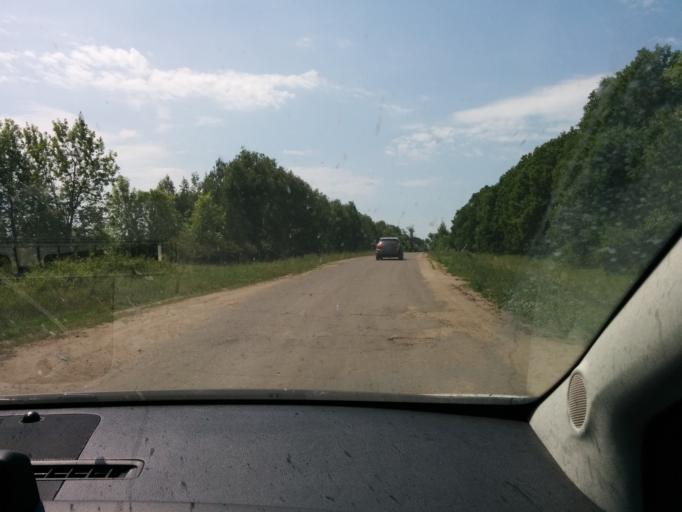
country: RU
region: Tambov
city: Morshansk
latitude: 53.6138
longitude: 41.8290
